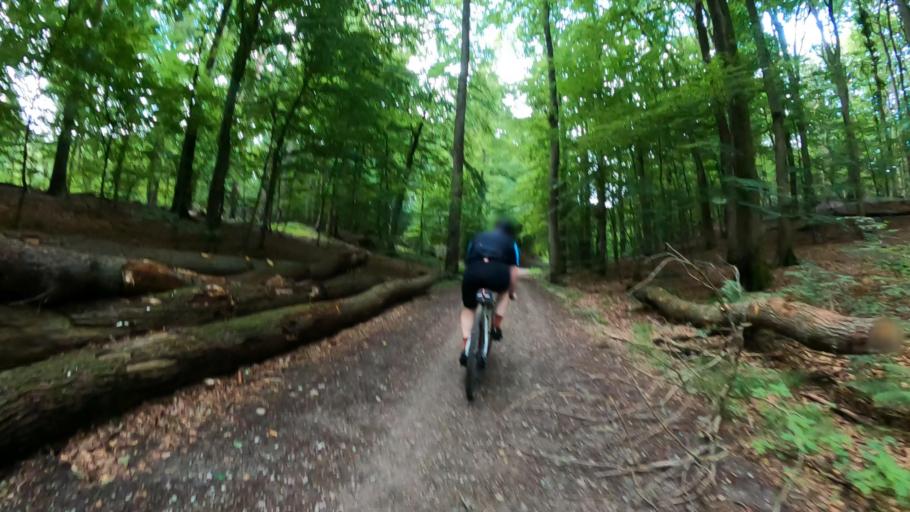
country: DE
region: Hamburg
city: Harburg
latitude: 53.4542
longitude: 9.9201
